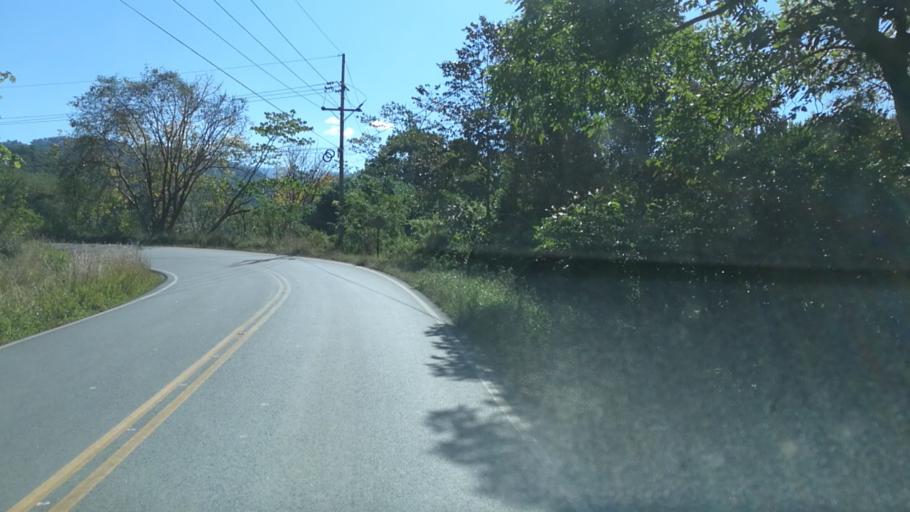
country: CR
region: San Jose
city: San Isidro
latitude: 9.2817
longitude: -83.8508
